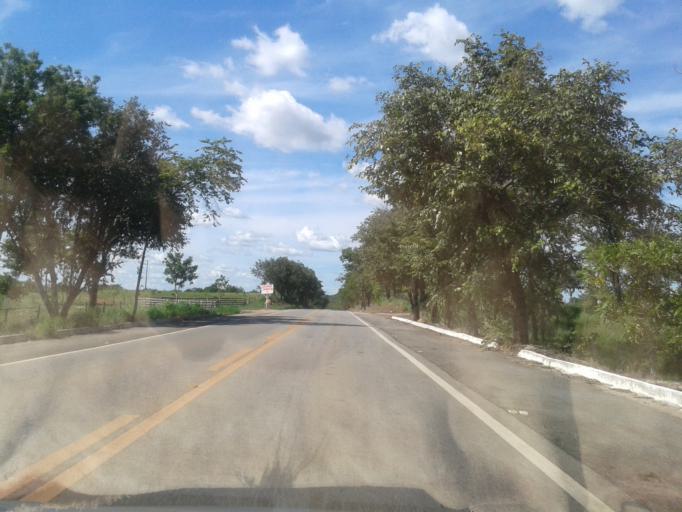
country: BR
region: Goias
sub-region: Itapuranga
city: Itapuranga
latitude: -15.4167
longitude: -50.3773
